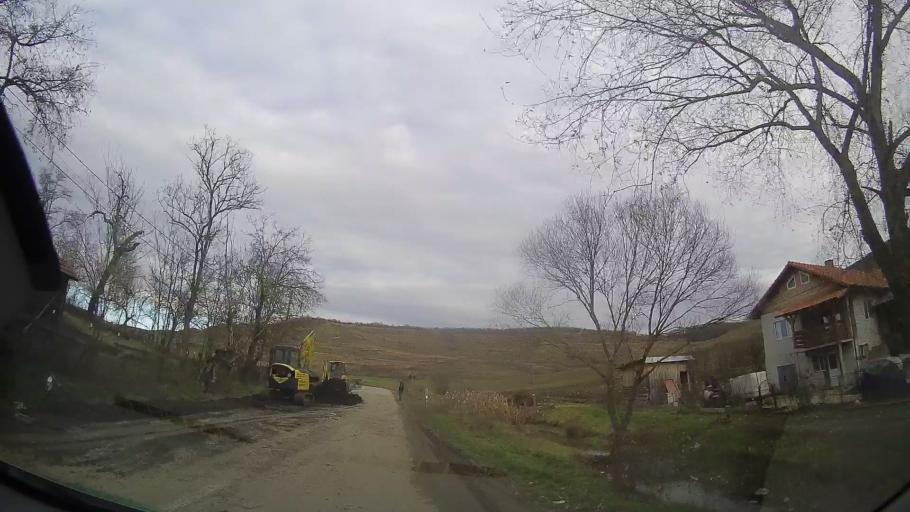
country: RO
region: Bistrita-Nasaud
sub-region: Comuna Micestii de Campie
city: Micestii de Campie
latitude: 46.8368
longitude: 24.3038
